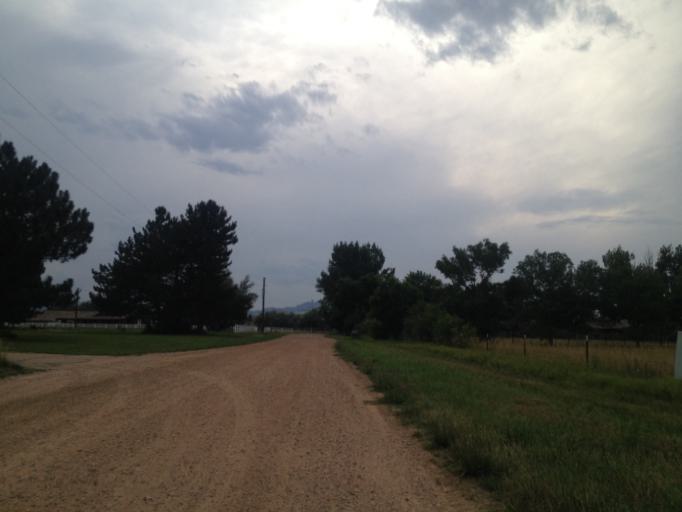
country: US
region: Colorado
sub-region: Boulder County
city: Louisville
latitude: 39.9525
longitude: -105.1340
